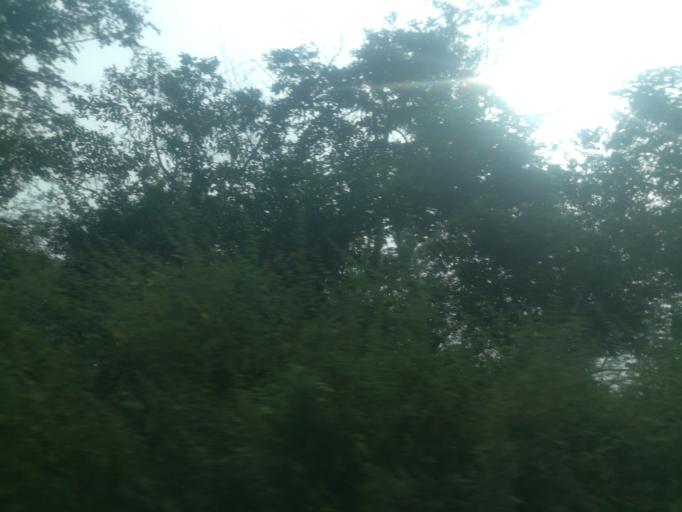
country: NG
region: Ogun
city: Ayetoro
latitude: 7.2909
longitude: 3.0805
